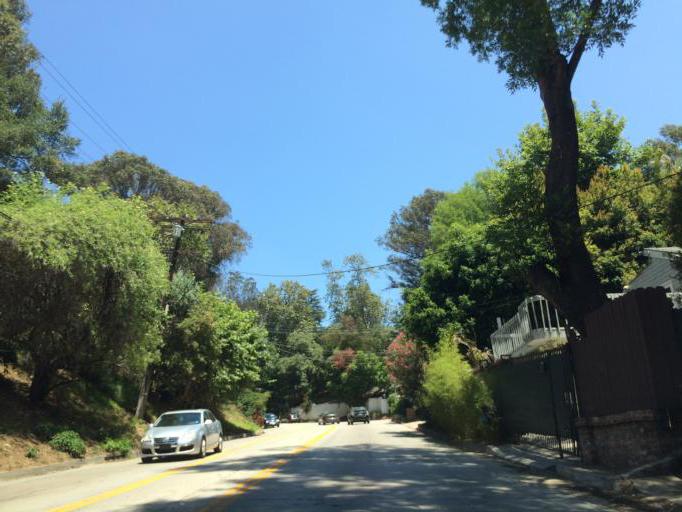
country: US
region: California
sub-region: Los Angeles County
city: West Hollywood
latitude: 34.1113
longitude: -118.3733
